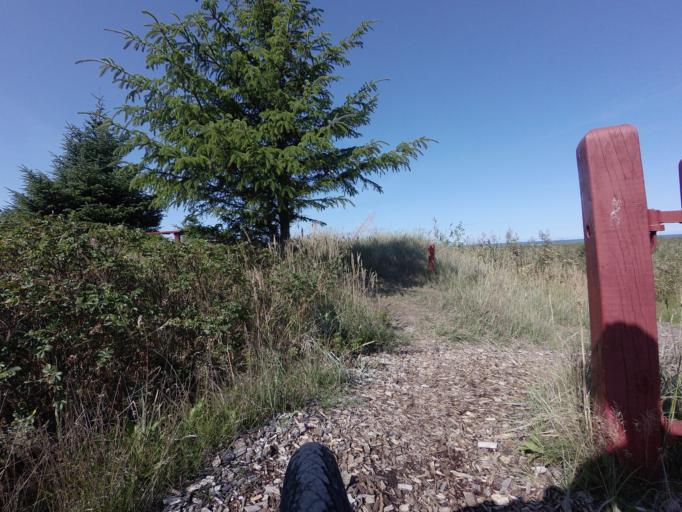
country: DK
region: North Denmark
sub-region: Hjorring Kommune
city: Hirtshals
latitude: 57.5879
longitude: 10.0771
